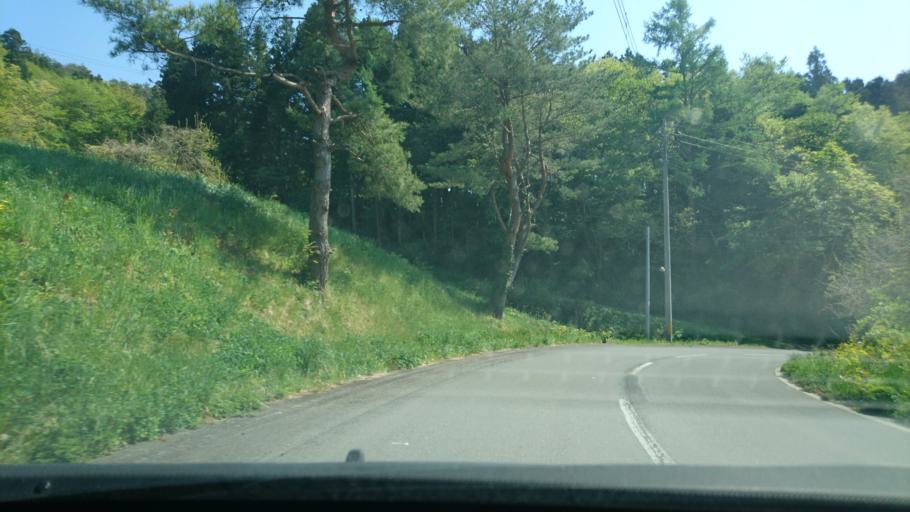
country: JP
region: Iwate
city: Ichinoseki
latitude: 38.9297
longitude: 141.2794
